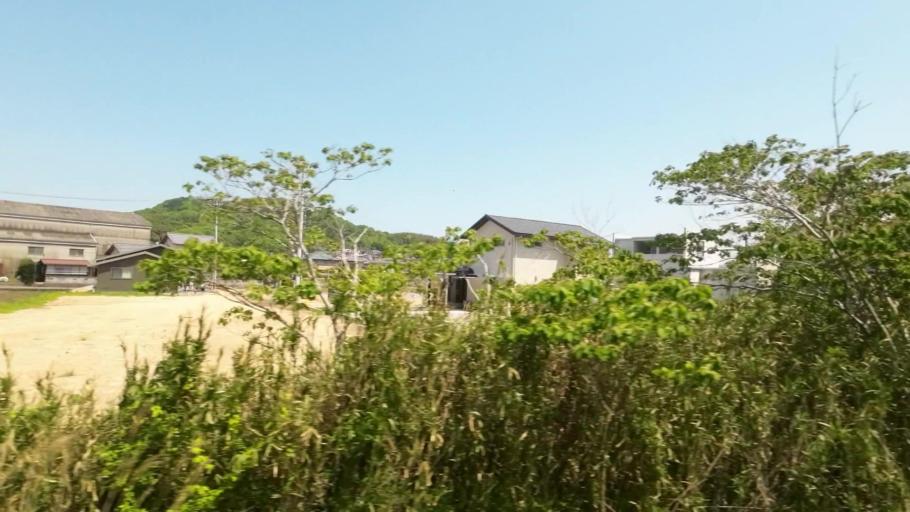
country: JP
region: Ehime
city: Hojo
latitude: 34.0963
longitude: 132.9538
